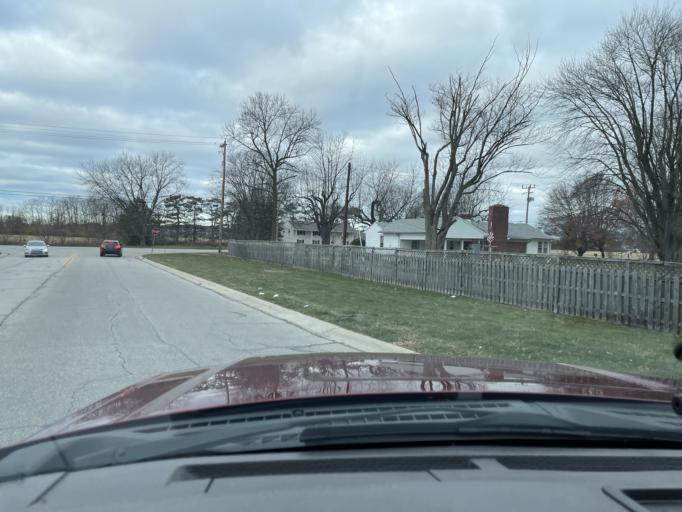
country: US
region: Indiana
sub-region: Hendricks County
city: Avon
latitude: 39.7650
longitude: -86.3609
